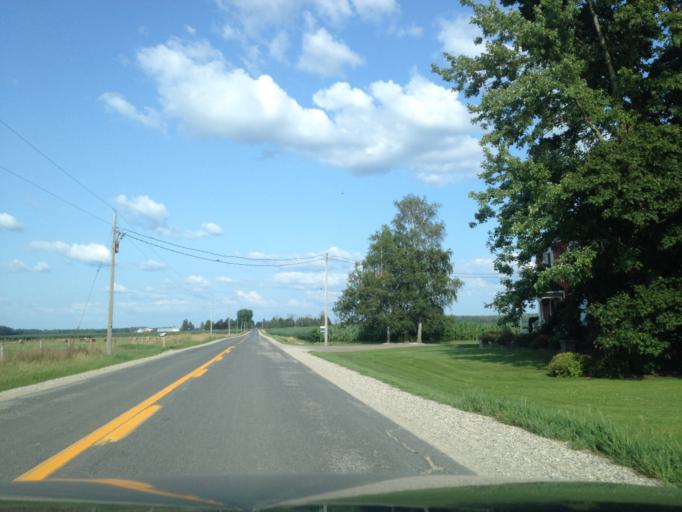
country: CA
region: Ontario
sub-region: Oxford County
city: Woodstock
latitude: 42.9680
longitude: -80.7293
